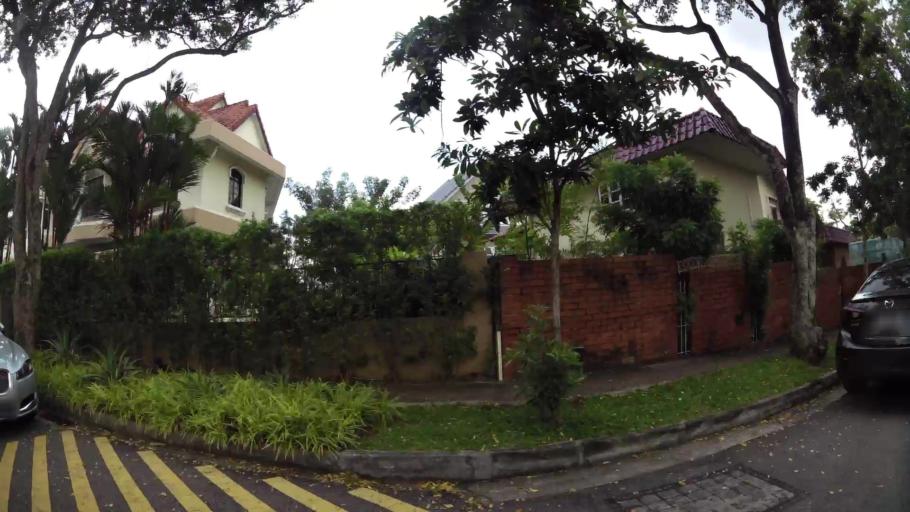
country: SG
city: Singapore
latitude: 1.3463
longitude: 103.8655
